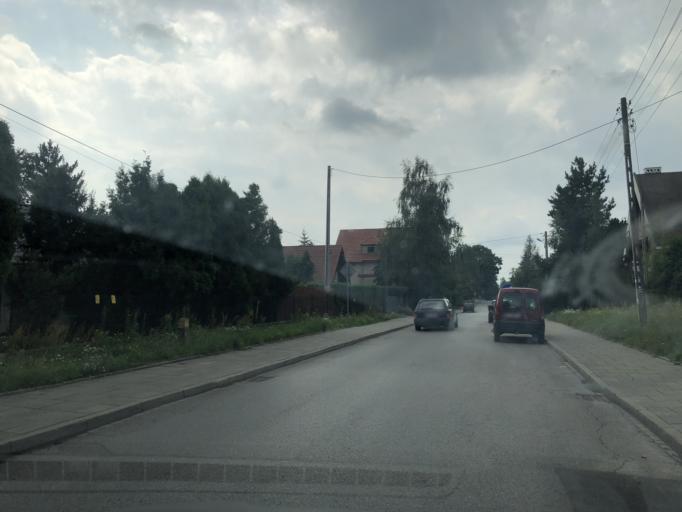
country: PL
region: Lesser Poland Voivodeship
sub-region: Powiat krakowski
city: Libertow
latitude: 50.0041
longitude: 19.9265
